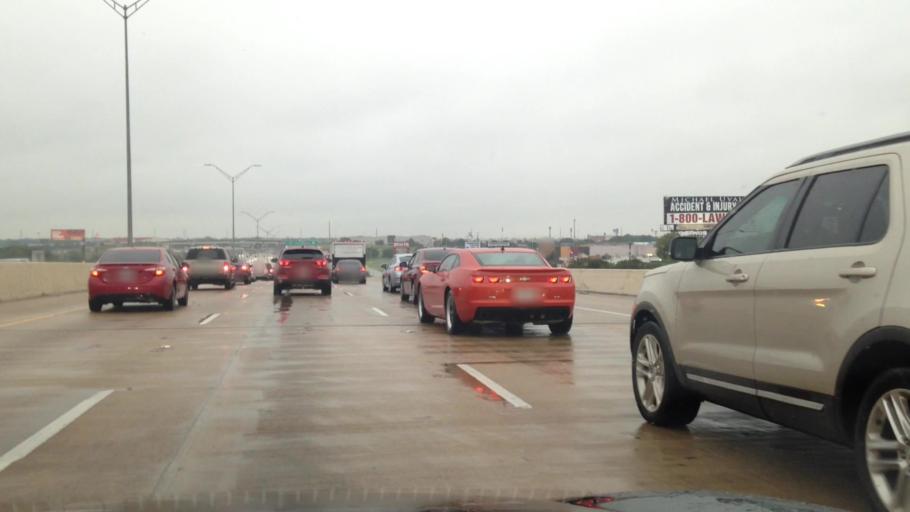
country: US
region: Texas
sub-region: Bexar County
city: Windcrest
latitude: 29.5153
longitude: -98.4105
